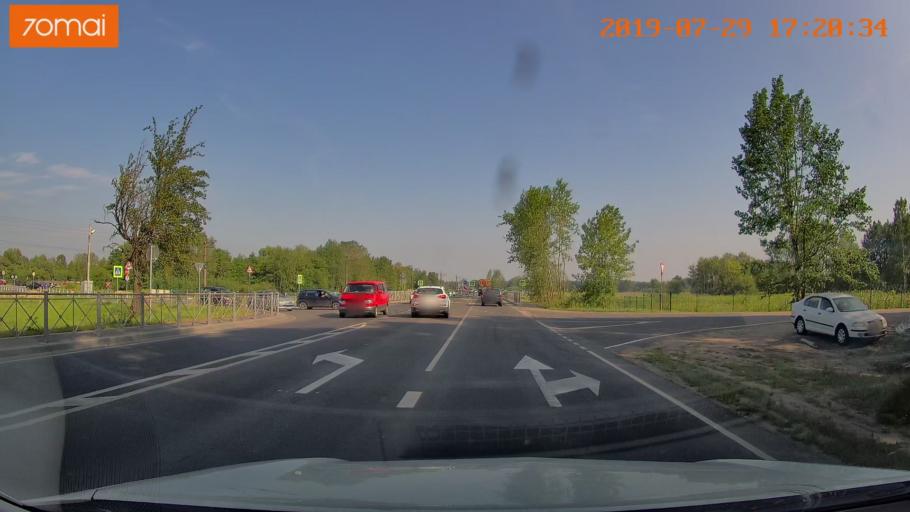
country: RU
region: Kaliningrad
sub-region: Gorod Kaliningrad
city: Kaliningrad
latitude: 54.7692
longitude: 20.4271
